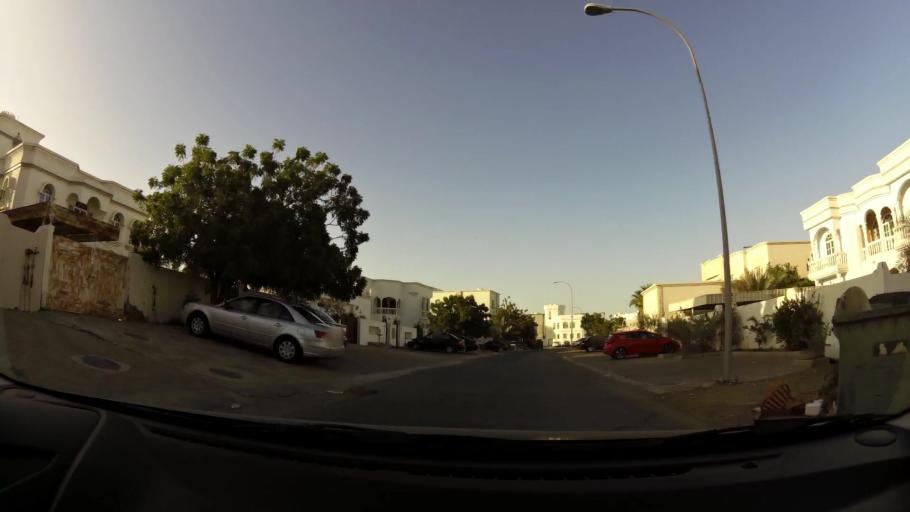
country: OM
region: Muhafazat Masqat
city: As Sib al Jadidah
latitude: 23.6076
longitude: 58.2227
